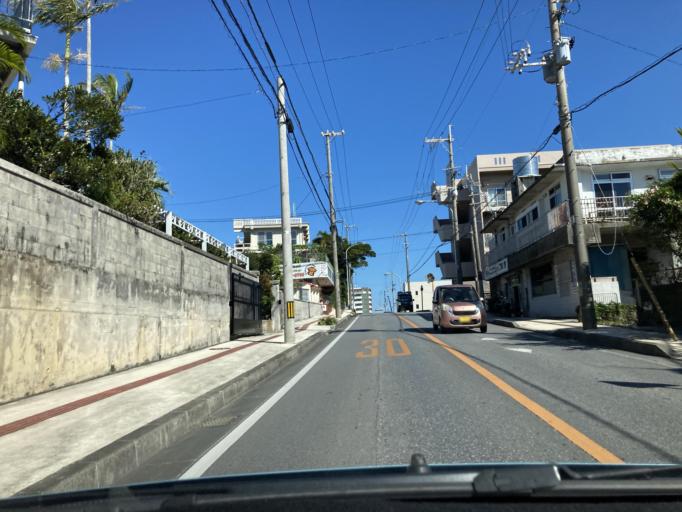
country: JP
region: Okinawa
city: Okinawa
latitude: 26.3296
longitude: 127.8040
